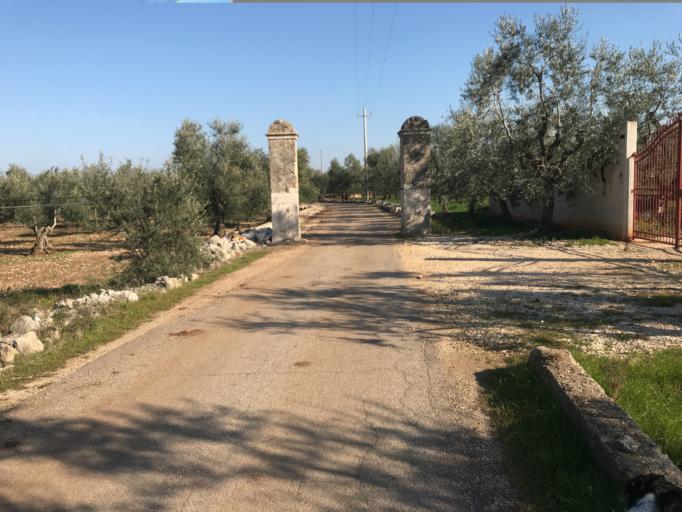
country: IT
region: Apulia
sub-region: Provincia di Bari
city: Corato
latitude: 41.1646
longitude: 16.4358
